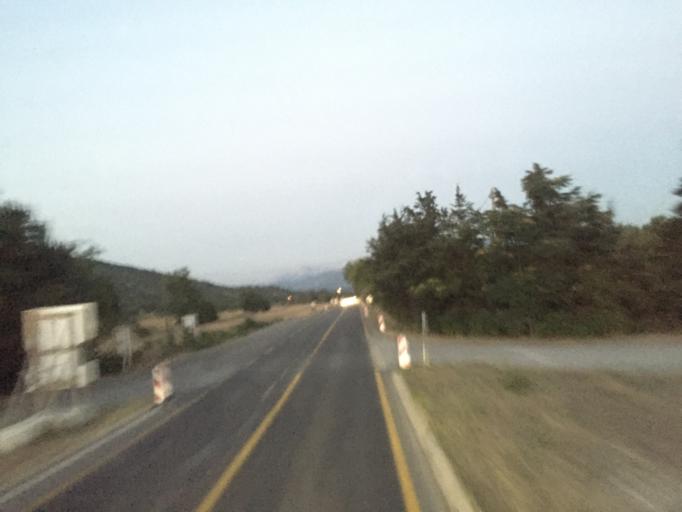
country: FR
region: Provence-Alpes-Cote d'Azur
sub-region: Departement des Alpes-de-Haute-Provence
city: Mallemoisson
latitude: 44.0342
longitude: 6.1005
